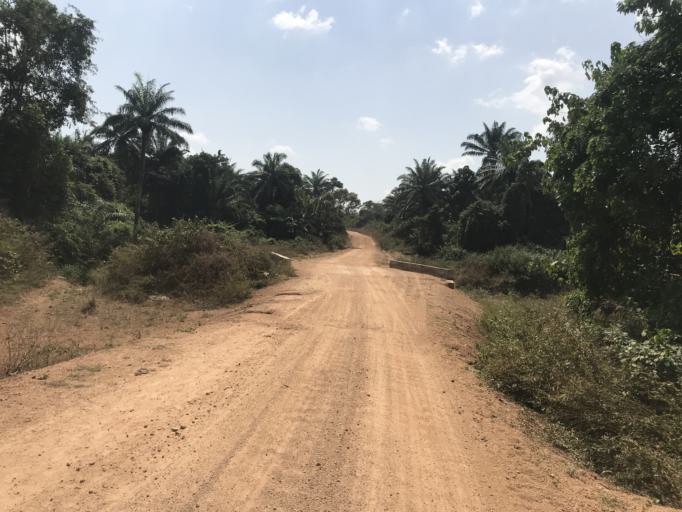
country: NG
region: Osun
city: Ifon
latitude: 7.9545
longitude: 4.4942
